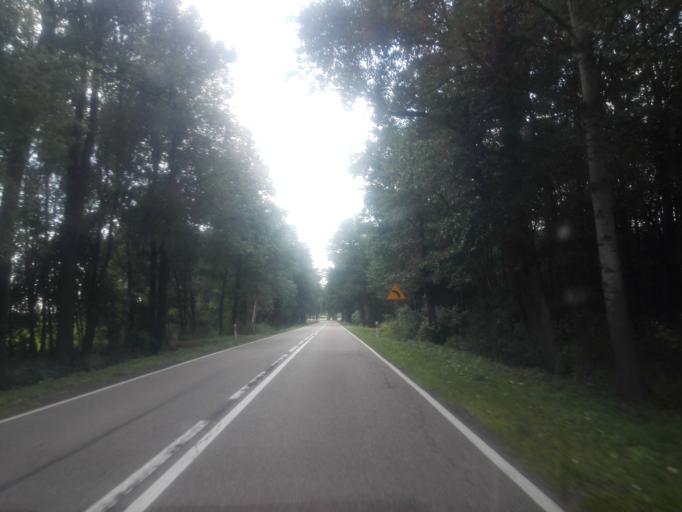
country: PL
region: Podlasie
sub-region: Powiat sejnenski
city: Krasnopol
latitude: 53.9463
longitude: 23.1914
